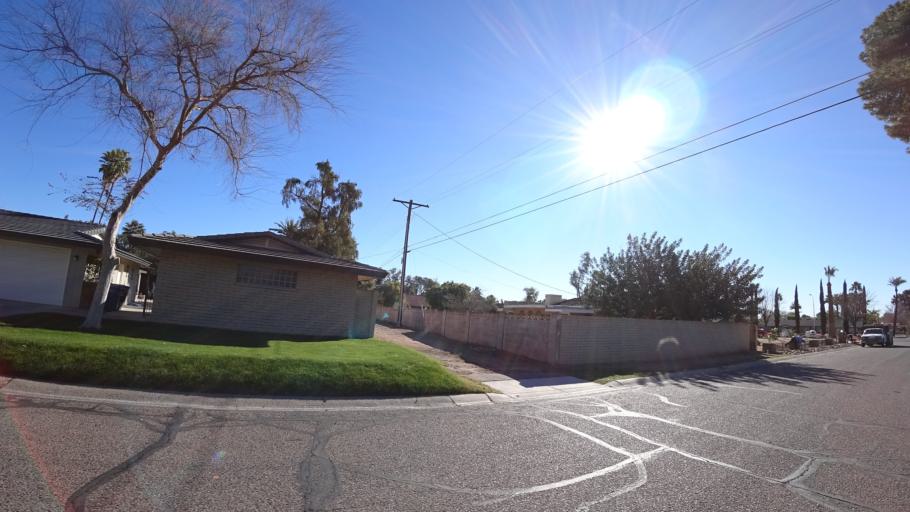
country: US
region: Arizona
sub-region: Maricopa County
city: Paradise Valley
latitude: 33.5108
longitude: -112.0019
